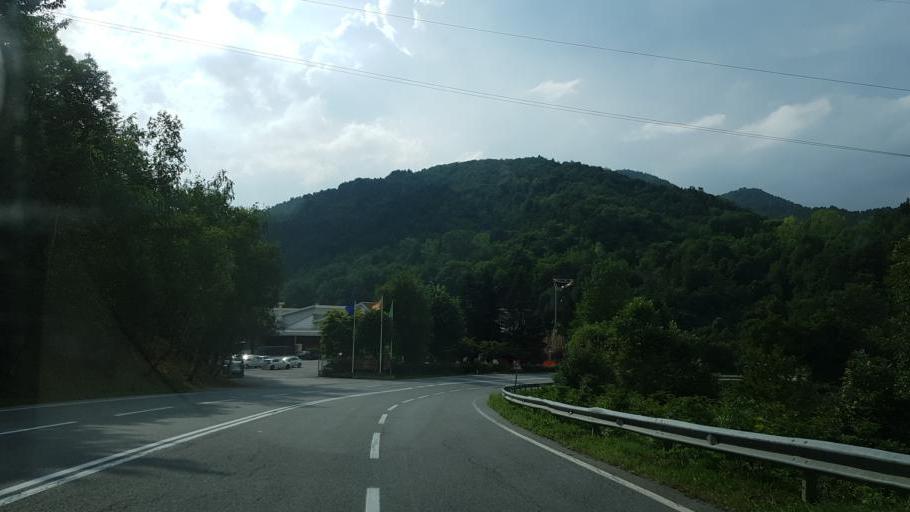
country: IT
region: Piedmont
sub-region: Provincia di Cuneo
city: Vignolo
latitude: 44.3452
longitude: 7.4751
